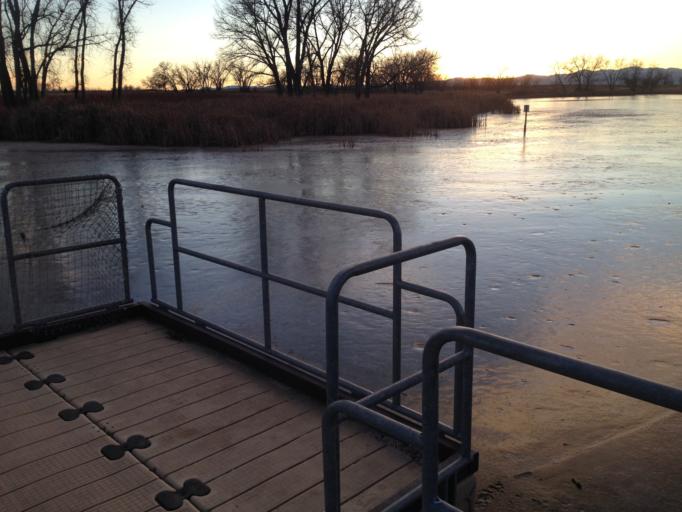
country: US
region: Colorado
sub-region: Adams County
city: Derby
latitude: 39.8142
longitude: -104.8528
